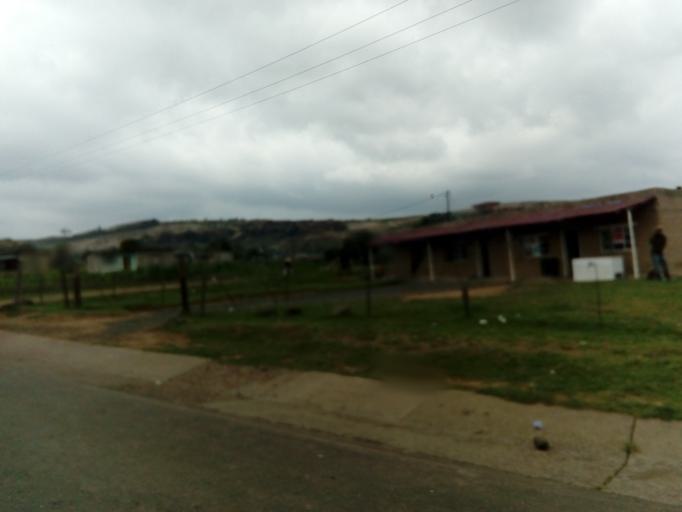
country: LS
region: Leribe
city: Leribe
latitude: -29.0280
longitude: 28.0247
